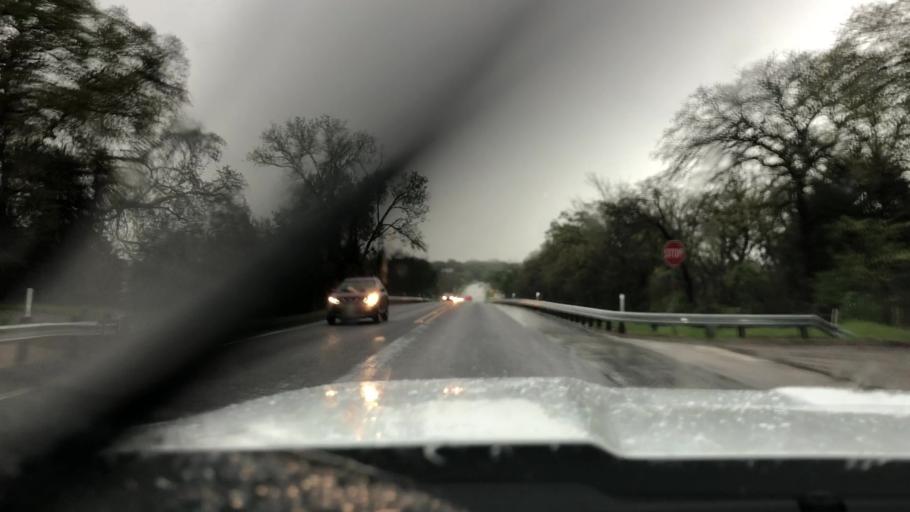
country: US
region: Texas
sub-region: Johnson County
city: Keene
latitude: 32.4510
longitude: -97.3037
